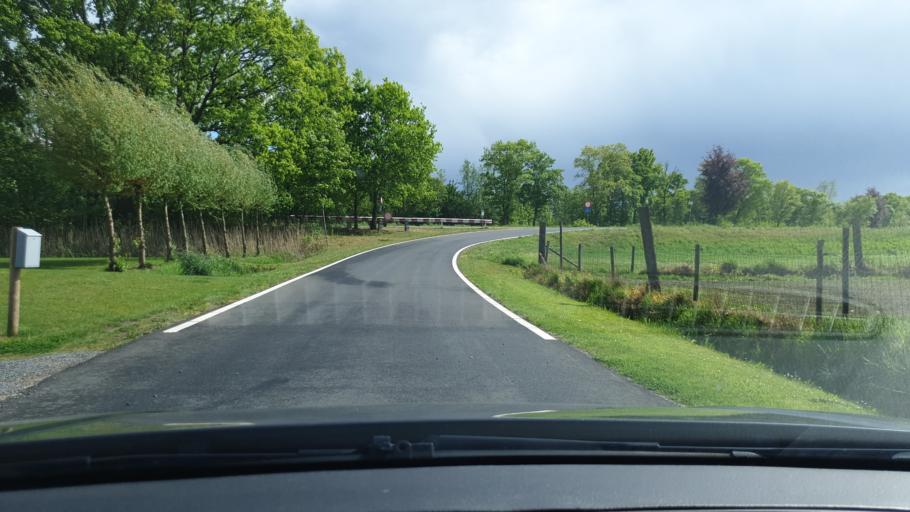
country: BE
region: Flanders
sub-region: Provincie Antwerpen
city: Geel
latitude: 51.1983
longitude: 4.9637
